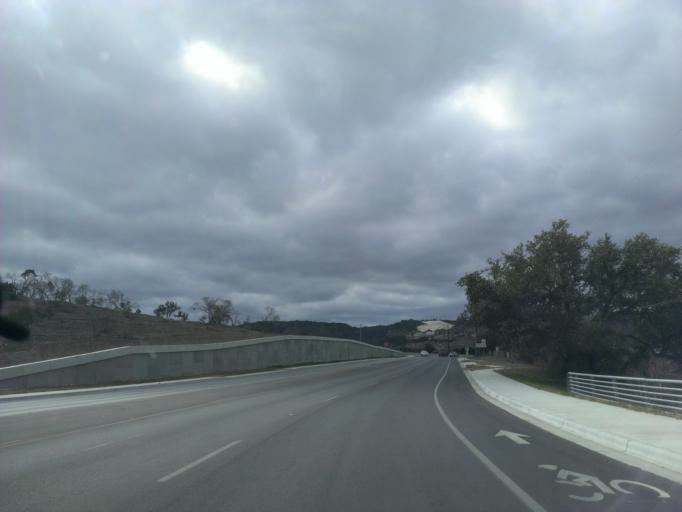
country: US
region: Texas
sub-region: Travis County
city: The Hills
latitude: 30.3335
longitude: -98.0239
